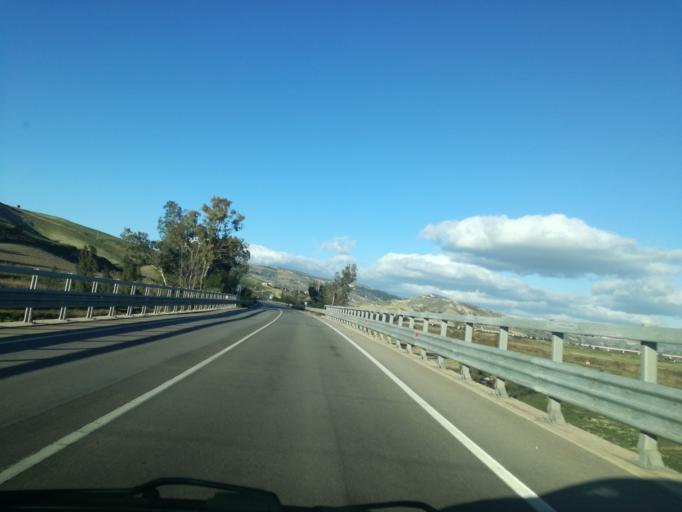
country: IT
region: Sicily
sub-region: Enna
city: Pietraperzia
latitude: 37.4433
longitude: 14.0993
